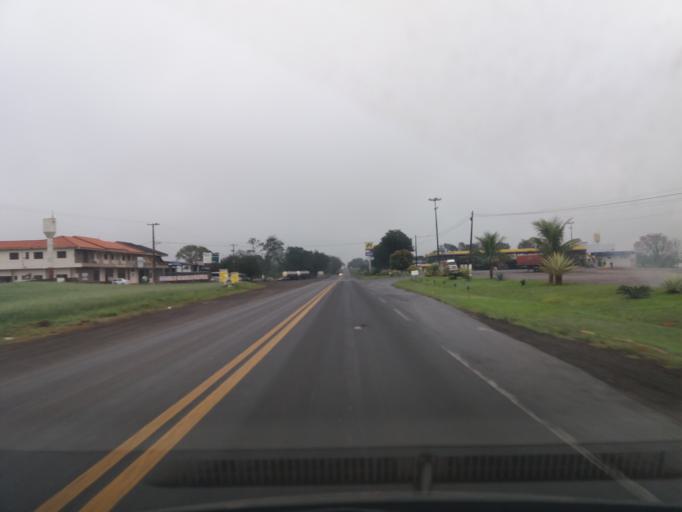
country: BR
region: Parana
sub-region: Ampere
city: Ampere
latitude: -25.8914
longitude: -53.4619
